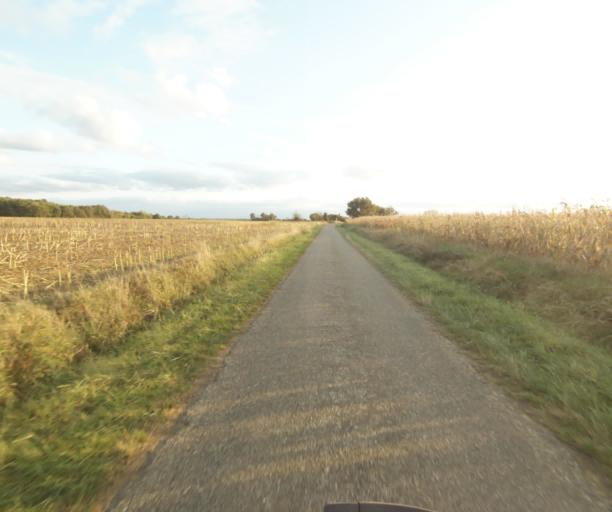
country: FR
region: Midi-Pyrenees
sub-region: Departement du Tarn-et-Garonne
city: Verdun-sur-Garonne
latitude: 43.8282
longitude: 1.1606
